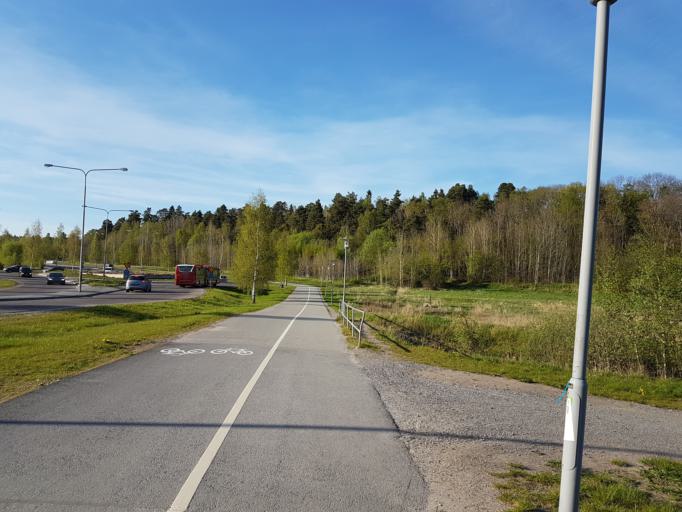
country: SE
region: Stockholm
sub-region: Solna Kommun
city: Rasunda
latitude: 59.3779
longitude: 17.9731
